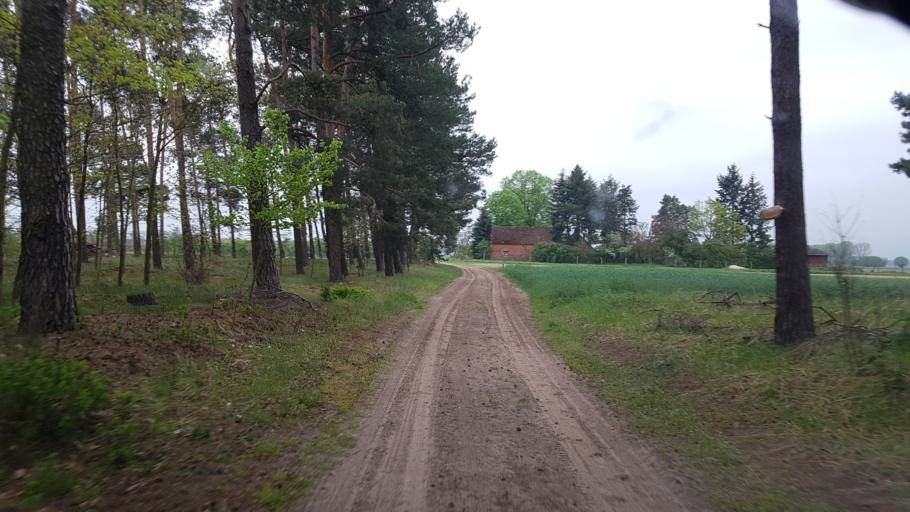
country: DE
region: Brandenburg
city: Schonewalde
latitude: 51.7030
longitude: 13.5633
